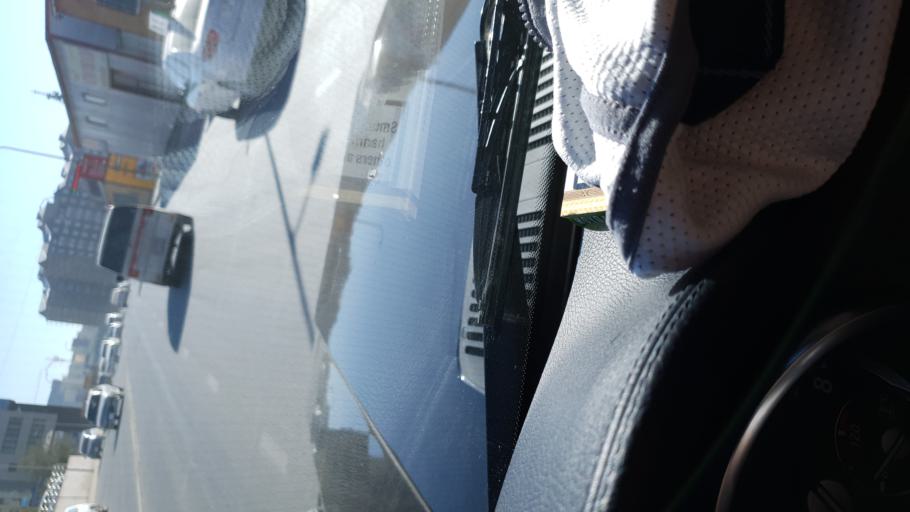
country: MN
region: Ulaanbaatar
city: Ulaanbaatar
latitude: 47.9249
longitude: 106.9466
